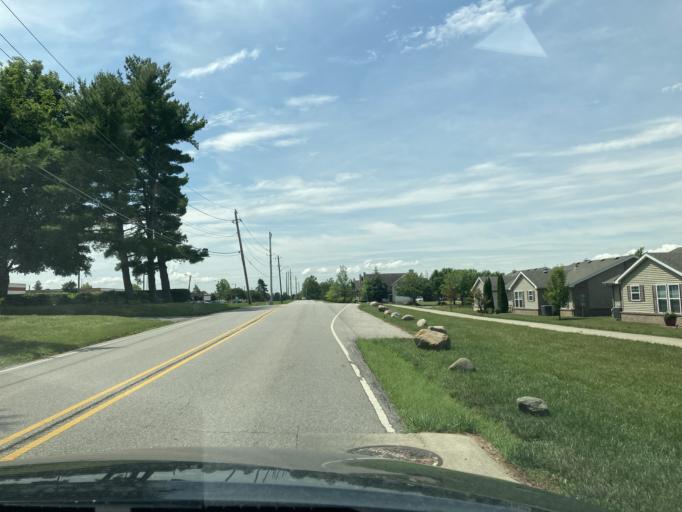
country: US
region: Indiana
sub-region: Marion County
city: Speedway
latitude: 39.8706
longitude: -86.2410
